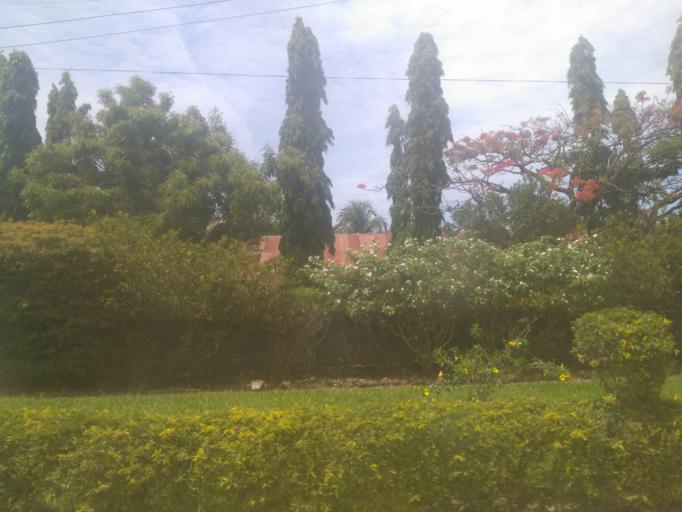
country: TZ
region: Zanzibar Urban/West
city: Zanzibar
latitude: -6.2120
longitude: 39.2110
